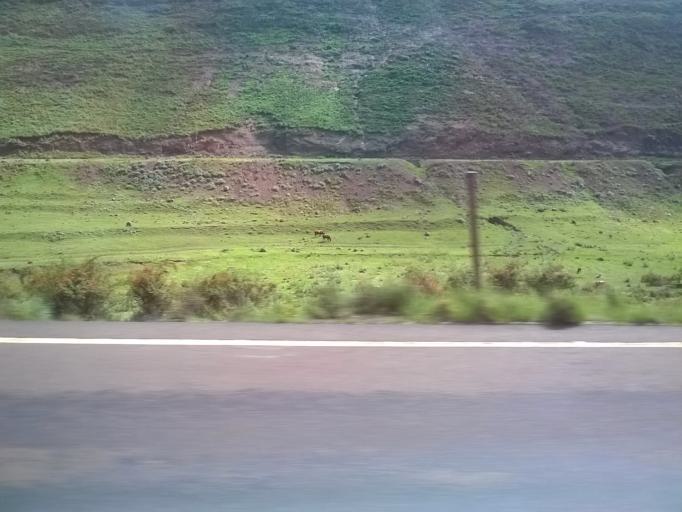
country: LS
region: Thaba-Tseka
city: Thaba-Tseka
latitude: -29.1589
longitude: 28.4766
